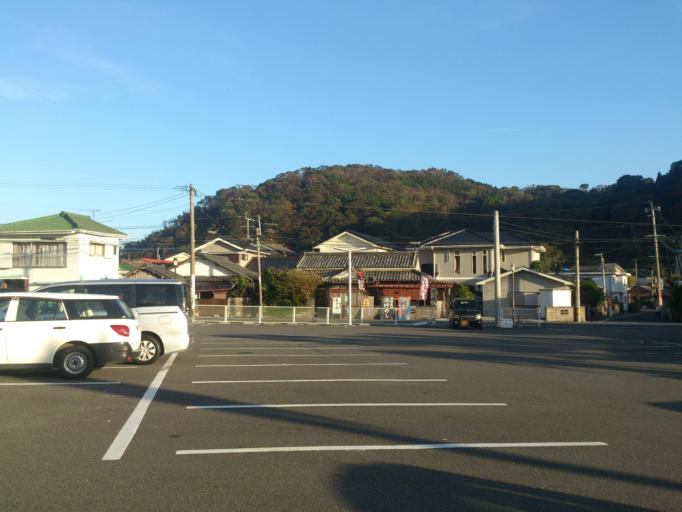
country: JP
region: Kagoshima
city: Ibusuki
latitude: 31.2029
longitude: 130.6346
